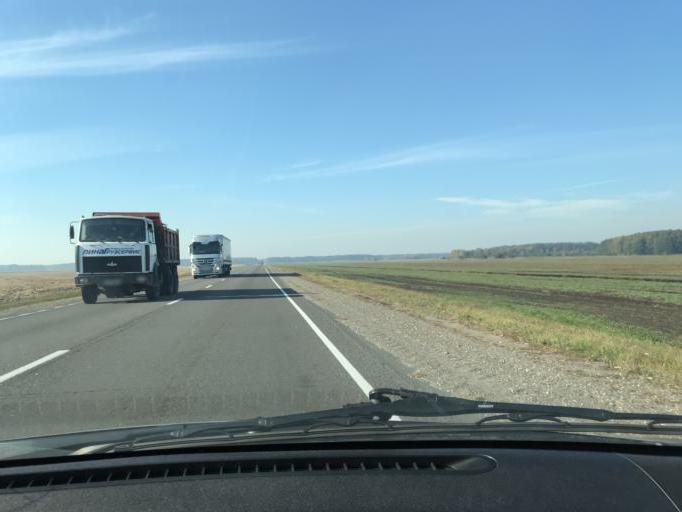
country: BY
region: Brest
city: Horad Luninyets
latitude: 52.3011
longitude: 26.4682
